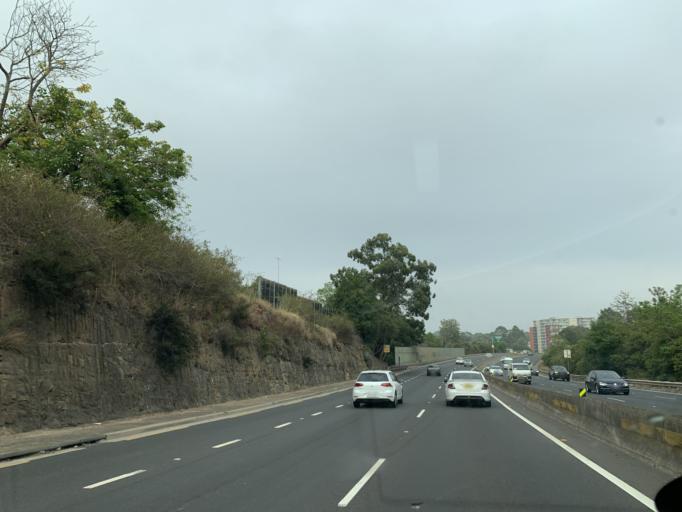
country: AU
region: New South Wales
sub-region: Parramatta
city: Northmead
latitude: -33.7926
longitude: 151.0039
